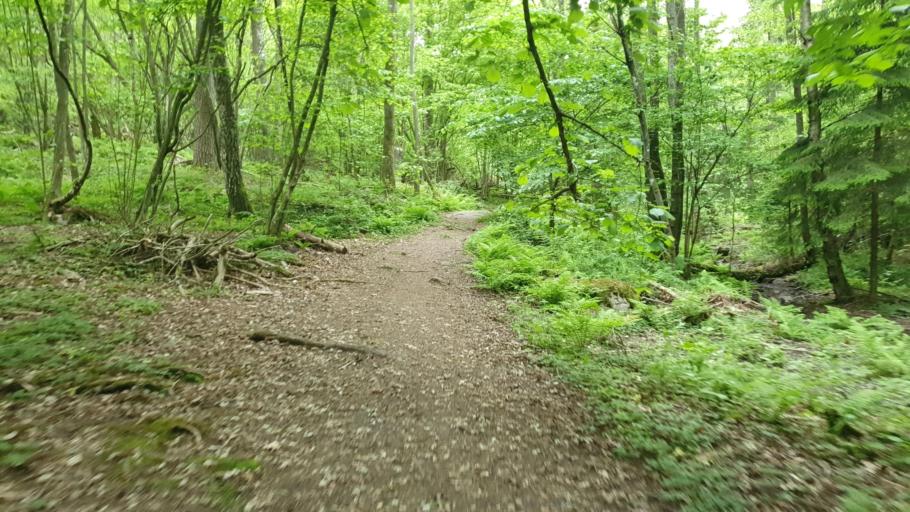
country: SE
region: Vaestra Goetaland
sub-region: Molndal
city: Kallered
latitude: 57.6133
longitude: 12.0552
